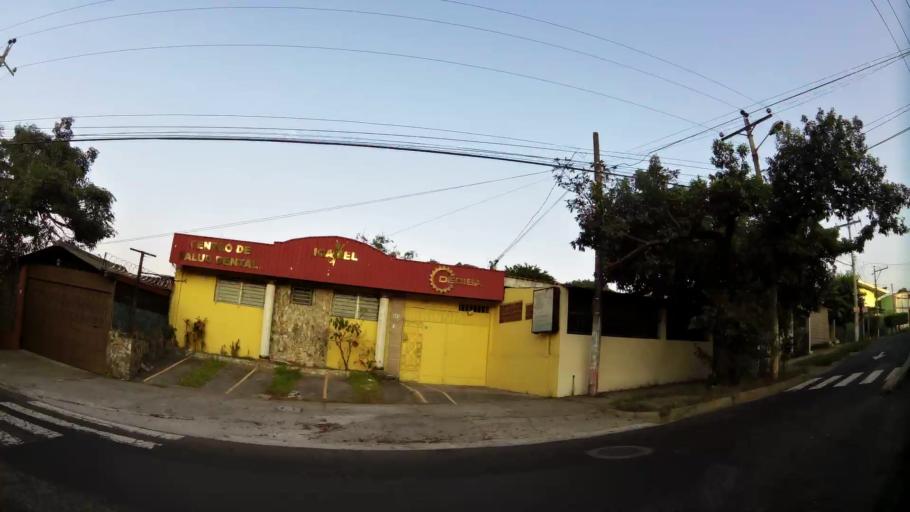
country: SV
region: San Salvador
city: San Salvador
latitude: 13.6808
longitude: -89.2111
